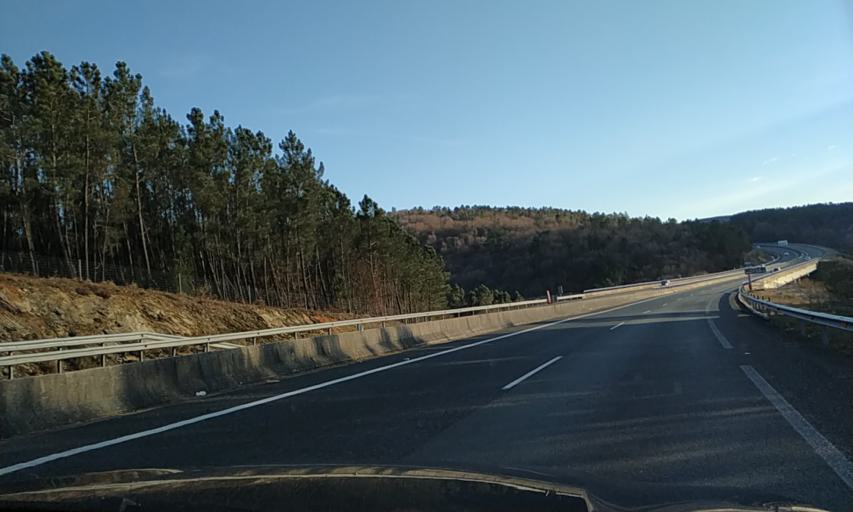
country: ES
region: Galicia
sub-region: Provincia de Pontevedra
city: Lalin
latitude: 42.6161
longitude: -8.0984
